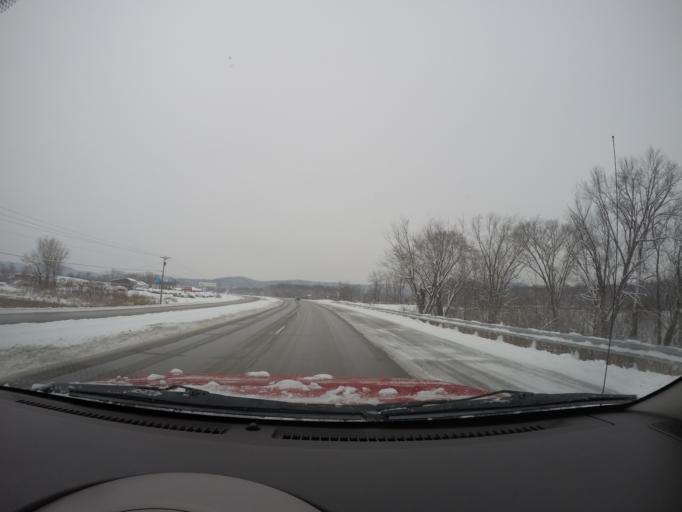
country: US
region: Minnesota
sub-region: Houston County
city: La Crescent
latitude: 43.8248
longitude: -91.2840
